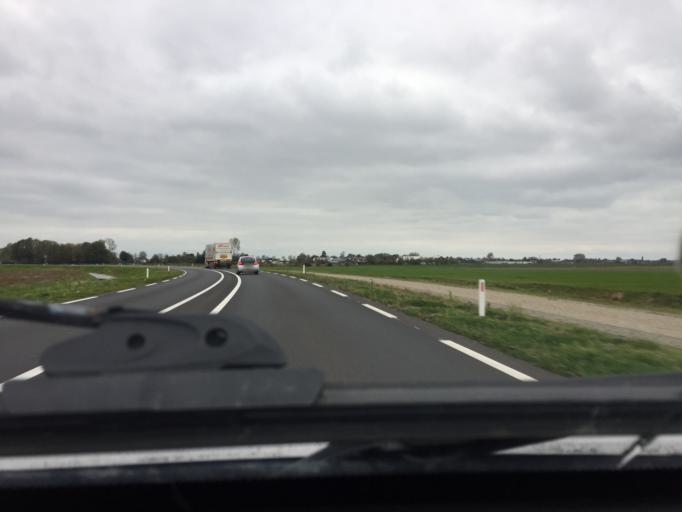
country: NL
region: North Holland
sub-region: Gemeente Heerhugowaard
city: Heerhugowaard
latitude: 52.6826
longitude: 4.8593
